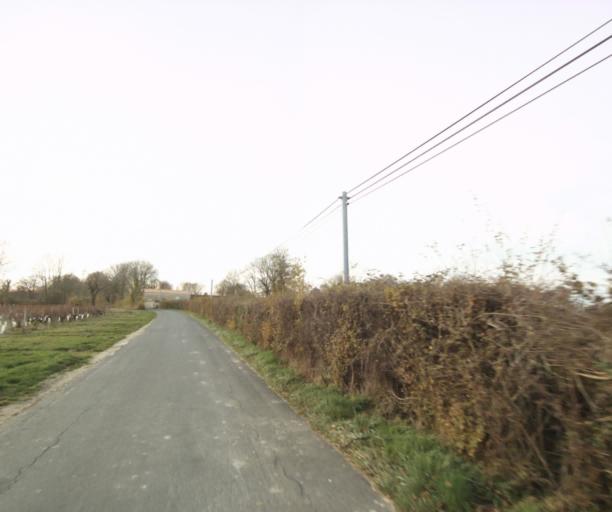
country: FR
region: Poitou-Charentes
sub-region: Departement de la Charente-Maritime
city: Fontcouverte
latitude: 45.7878
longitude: -0.5789
